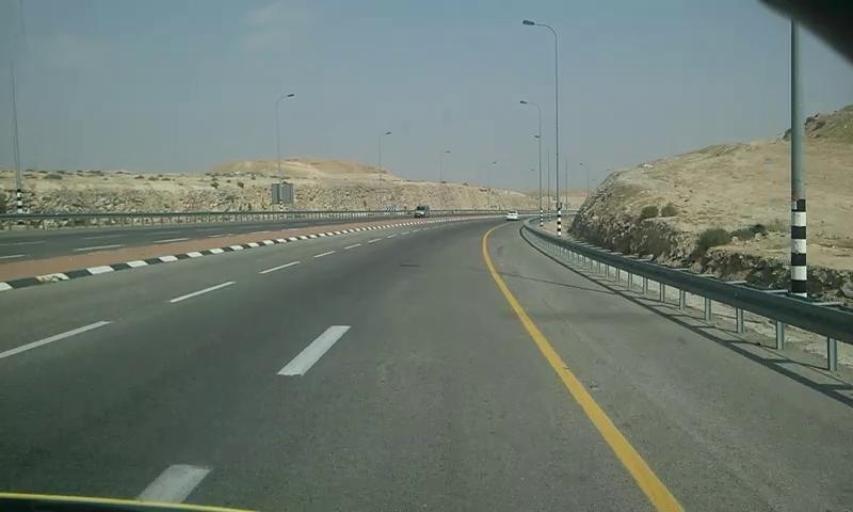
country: PS
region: West Bank
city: Jericho
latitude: 31.7987
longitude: 35.4293
